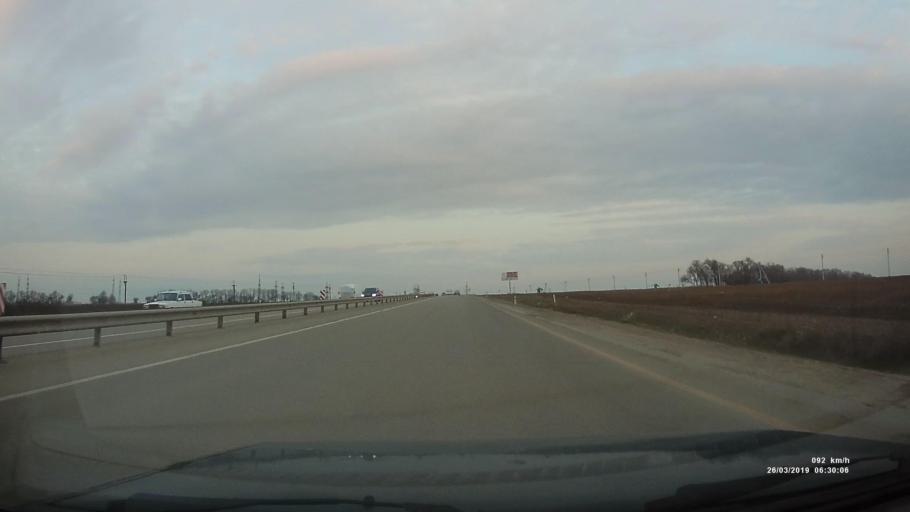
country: RU
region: Rostov
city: Krym
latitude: 47.2692
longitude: 39.5571
